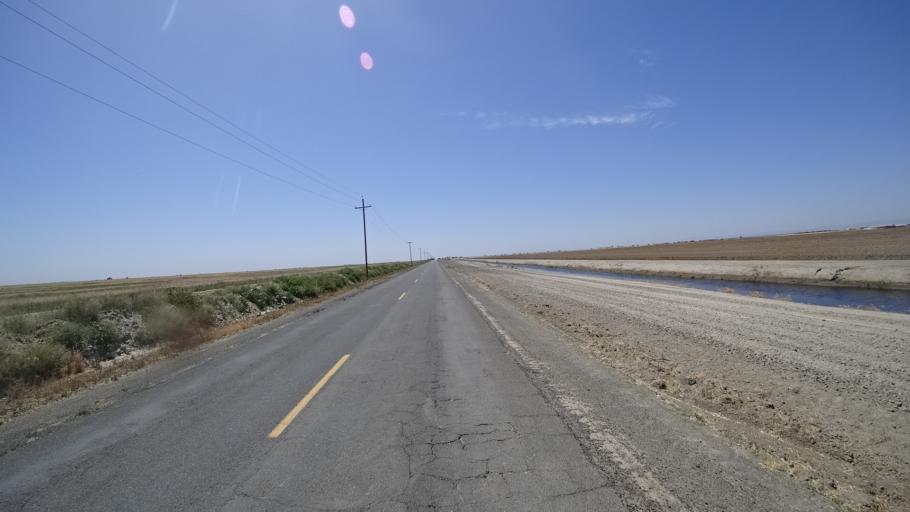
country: US
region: California
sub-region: Kings County
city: Stratford
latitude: 36.1660
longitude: -119.7174
